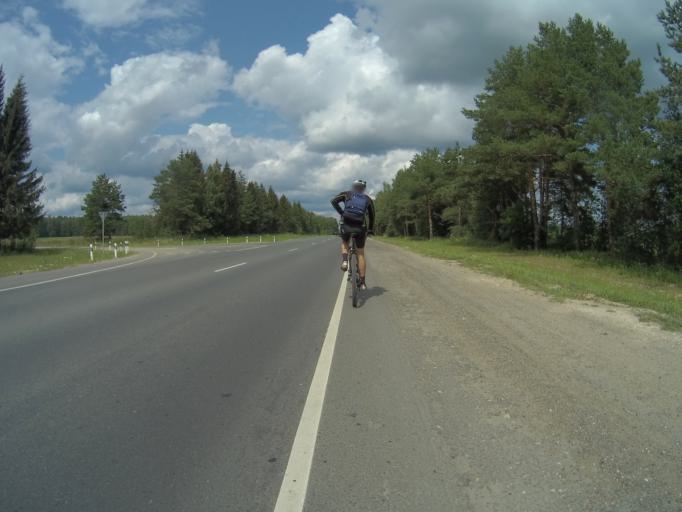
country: RU
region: Vladimir
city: Kideksha
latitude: 56.5728
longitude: 40.5545
